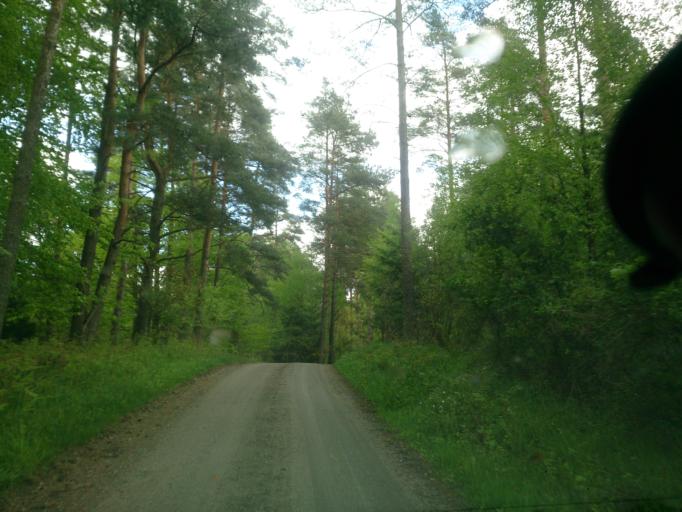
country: SE
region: Skane
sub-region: Sjobo Kommun
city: Sjoebo
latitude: 55.5601
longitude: 13.6937
